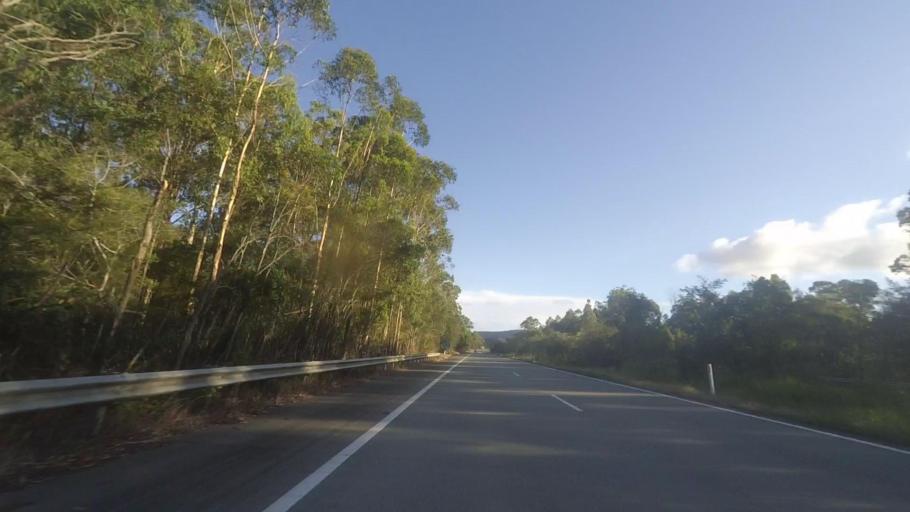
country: AU
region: New South Wales
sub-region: Great Lakes
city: Nabiac
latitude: -32.2441
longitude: 152.3214
